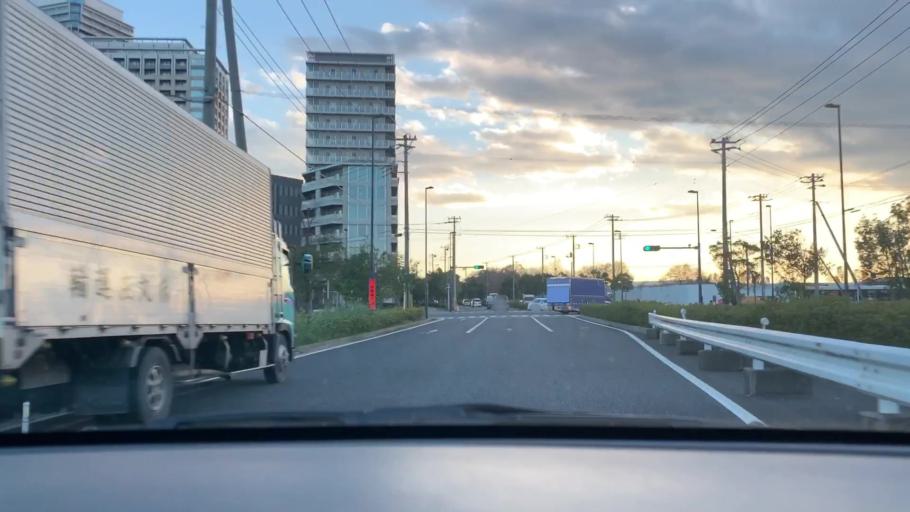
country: JP
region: Chiba
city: Kashiwa
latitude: 35.8986
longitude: 139.9496
